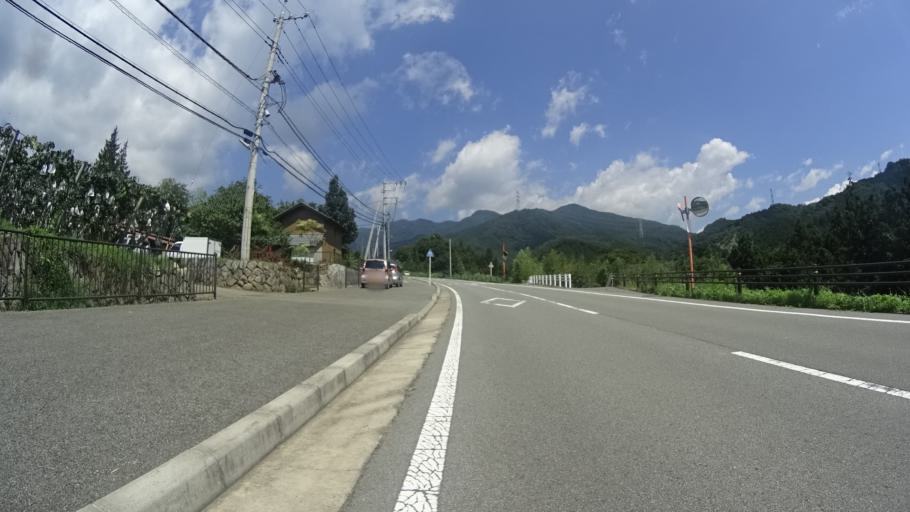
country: JP
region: Yamanashi
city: Enzan
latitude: 35.7603
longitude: 138.7061
